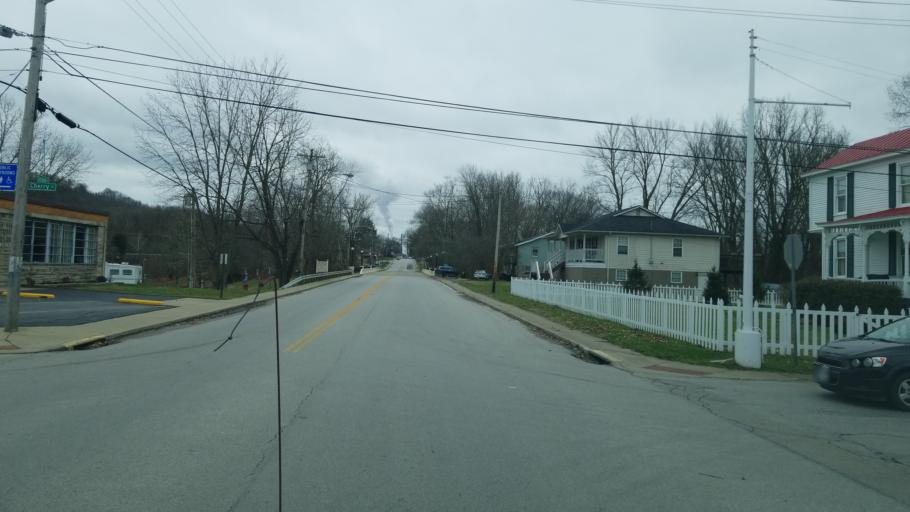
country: US
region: Ohio
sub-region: Brown County
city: Ripley
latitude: 38.7449
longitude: -83.8449
